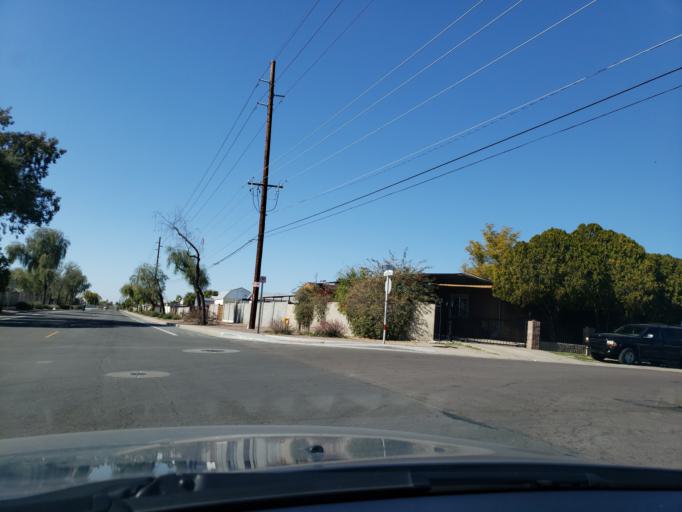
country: US
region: Arizona
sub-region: Maricopa County
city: Glendale
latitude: 33.6476
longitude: -112.0718
